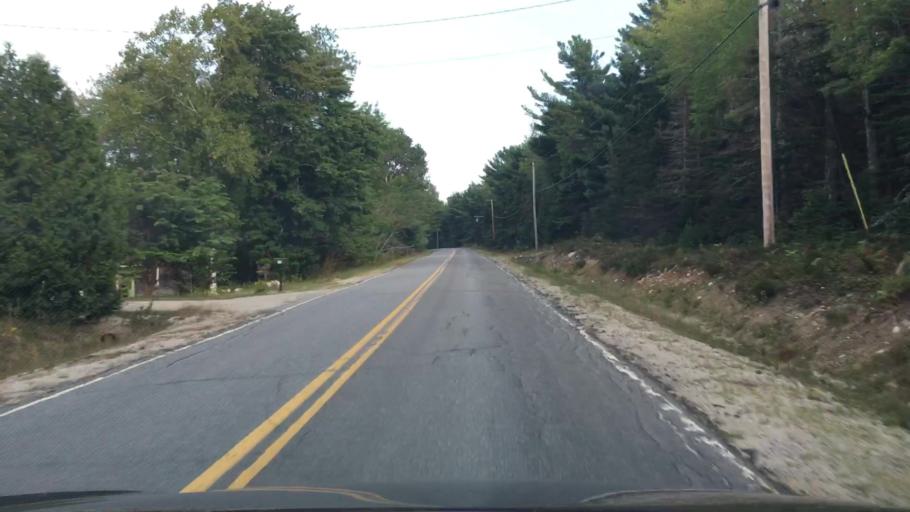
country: US
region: Maine
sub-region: Hancock County
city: Surry
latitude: 44.4984
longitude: -68.5454
